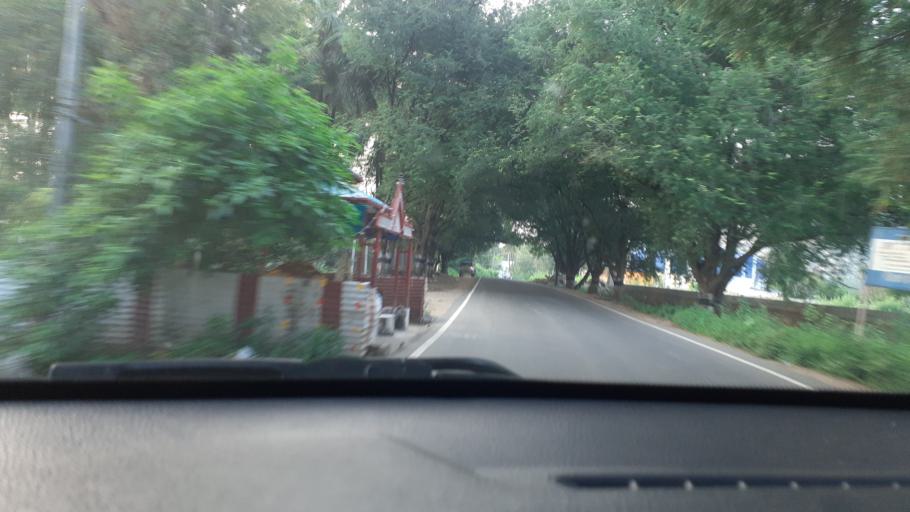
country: IN
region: Tamil Nadu
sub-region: Dindigul
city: Palani
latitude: 10.4301
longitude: 77.5256
